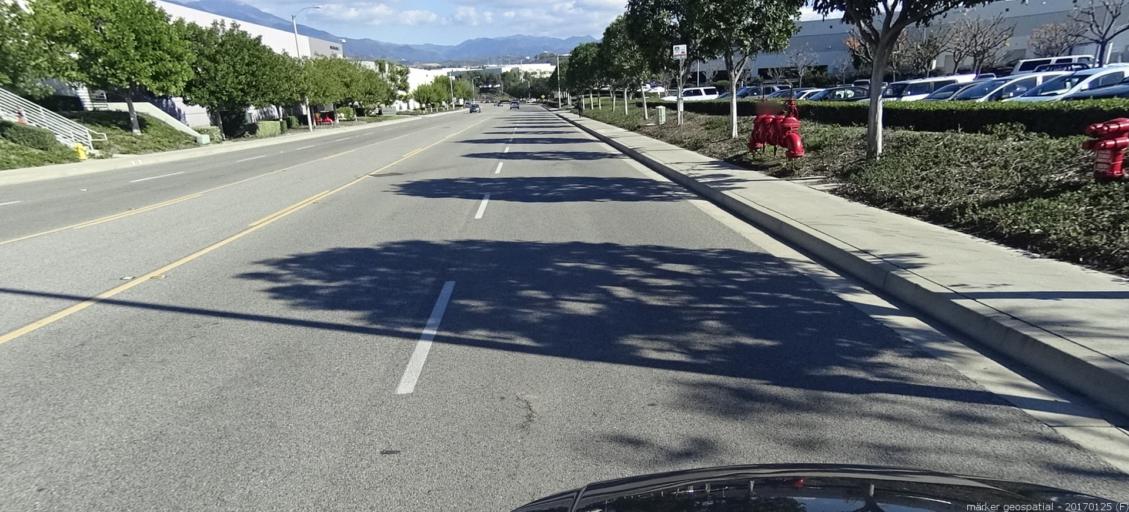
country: US
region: California
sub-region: Orange County
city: Lake Forest
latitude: 33.6644
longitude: -117.6795
